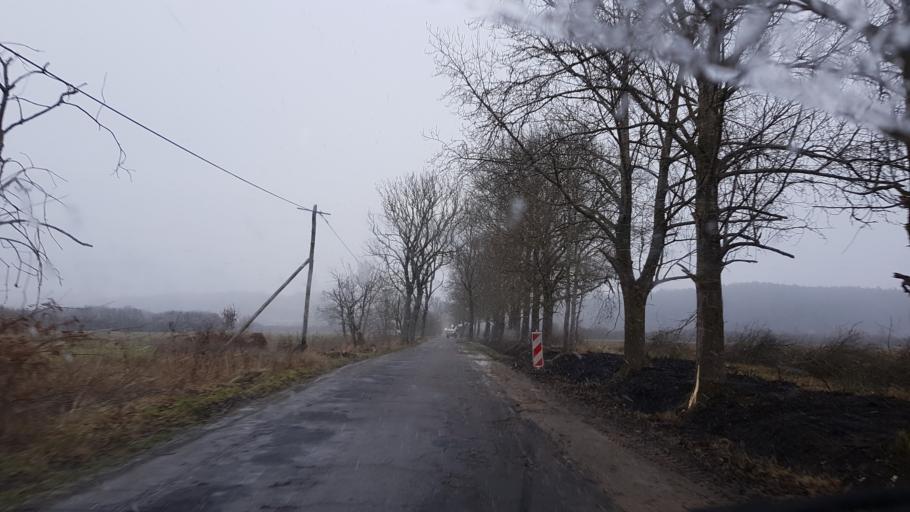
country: PL
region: West Pomeranian Voivodeship
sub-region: Powiat slawienski
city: Slawno
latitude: 54.2634
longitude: 16.5870
